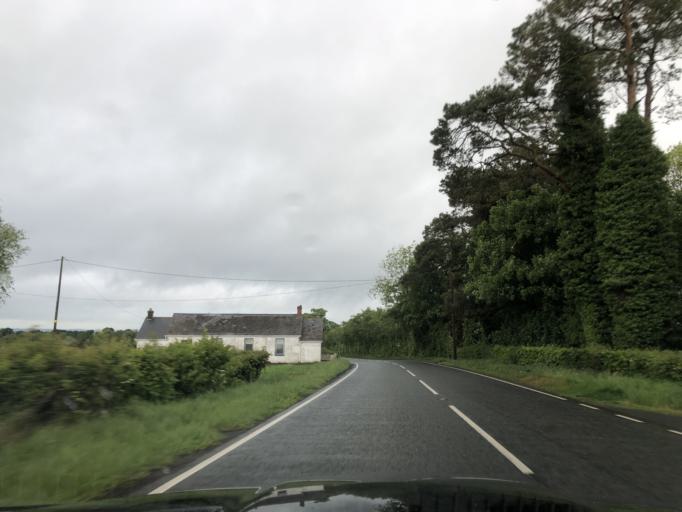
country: GB
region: Northern Ireland
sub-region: Antrim Borough
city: Antrim
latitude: 54.6719
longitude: -6.2203
